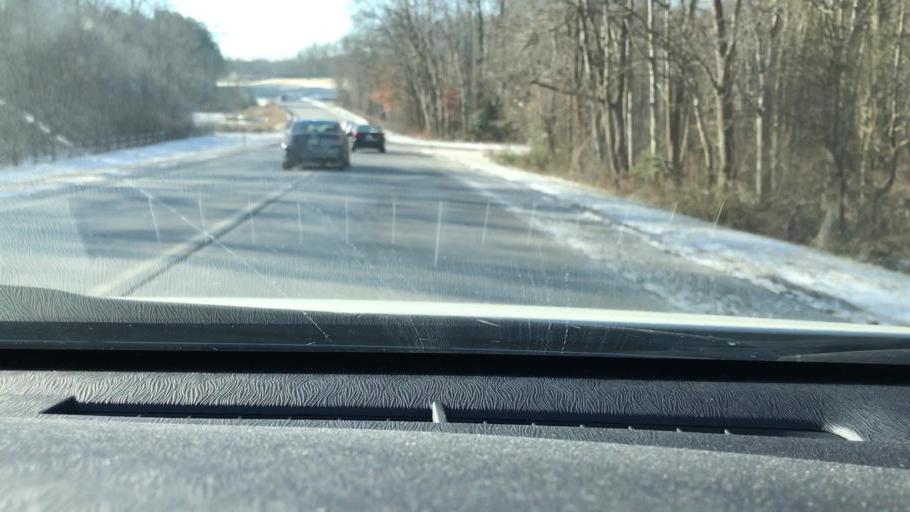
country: US
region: Maryland
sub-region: Prince George's County
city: Goddard
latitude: 39.0151
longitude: -76.8506
